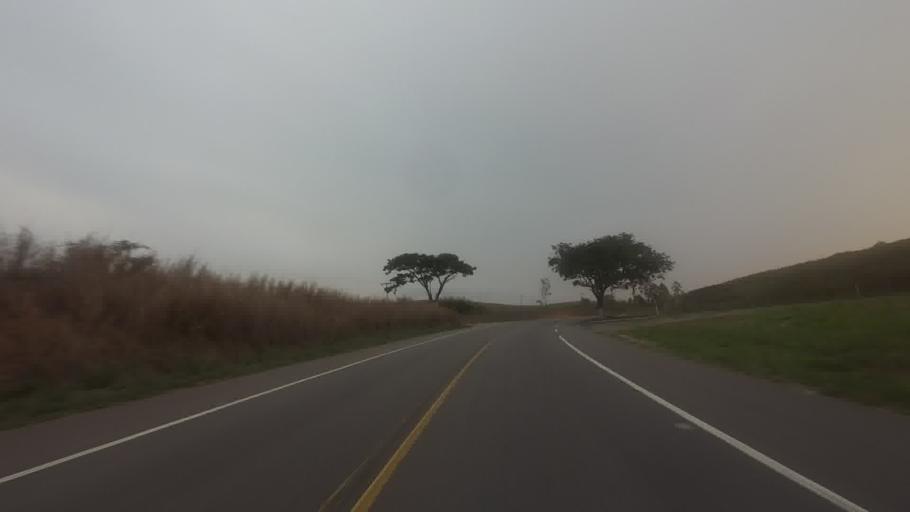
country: BR
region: Minas Gerais
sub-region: Recreio
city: Recreio
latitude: -21.6989
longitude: -42.4196
